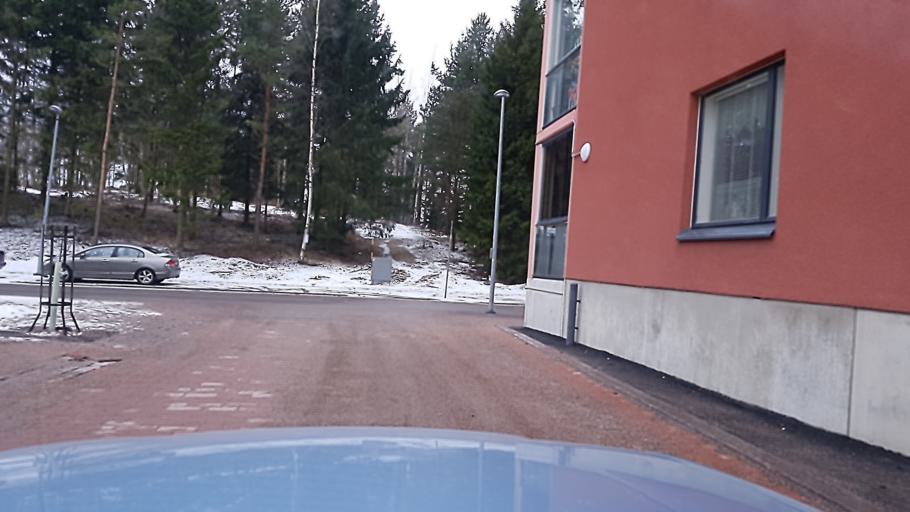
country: FI
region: Uusimaa
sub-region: Helsinki
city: Vantaa
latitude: 60.2604
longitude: 25.0683
